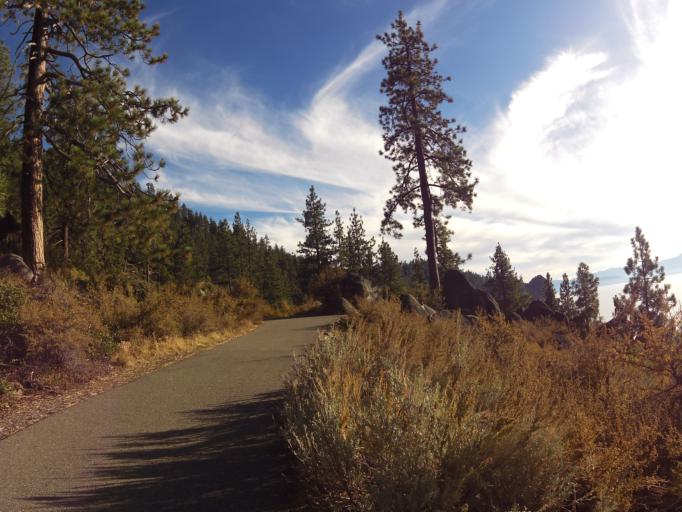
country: US
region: Nevada
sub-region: Douglas County
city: Kingsbury
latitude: 39.0581
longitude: -119.9435
